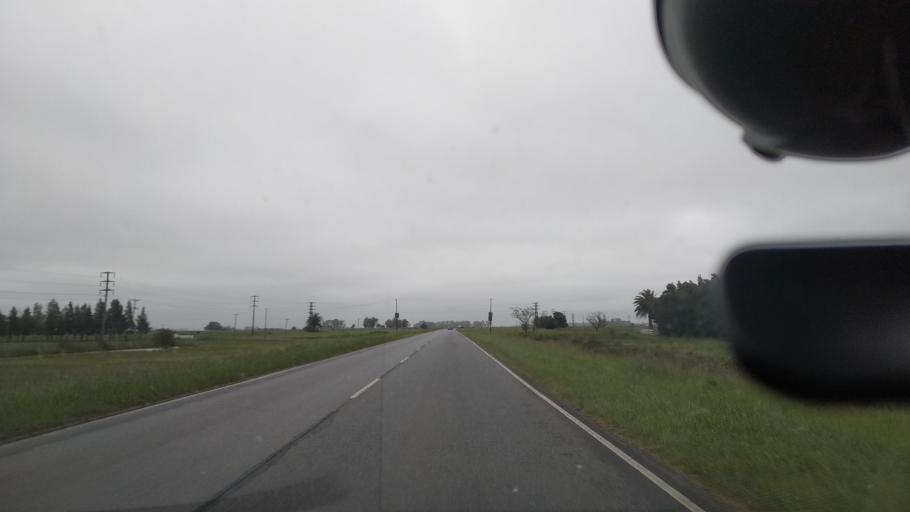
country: AR
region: Buenos Aires
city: Veronica
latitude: -35.3493
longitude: -57.4347
